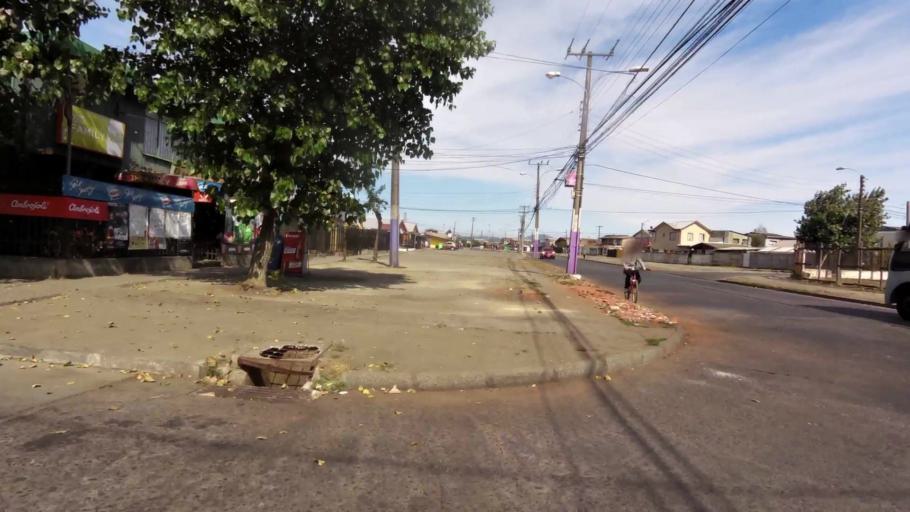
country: CL
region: Biobio
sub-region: Provincia de Concepcion
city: Talcahuano
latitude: -36.7847
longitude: -73.1065
